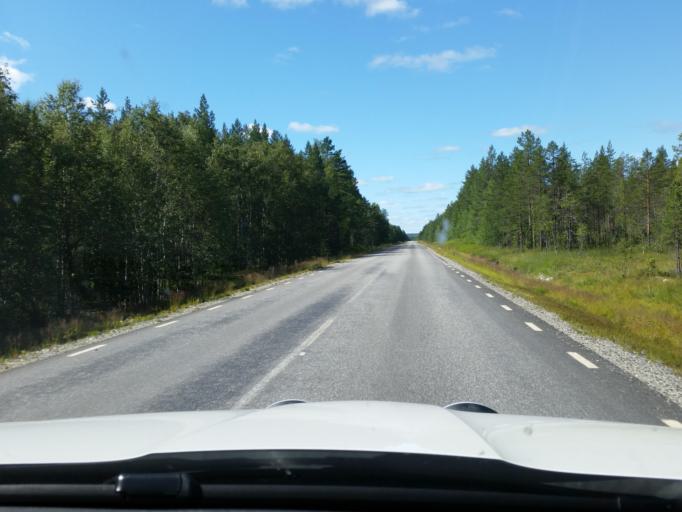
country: SE
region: Norrbotten
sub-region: Pitea Kommun
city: Roknas
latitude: 65.2007
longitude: 21.1547
